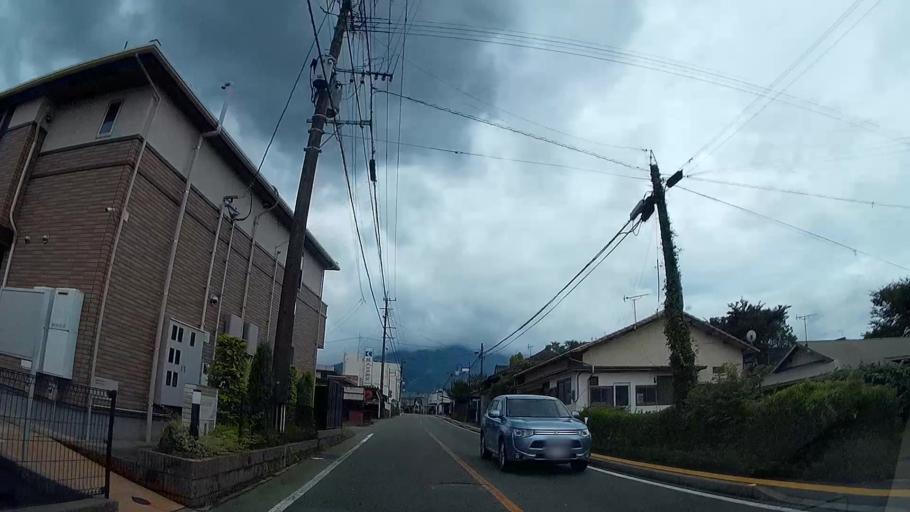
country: JP
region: Kumamoto
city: Aso
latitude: 32.9430
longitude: 131.1176
